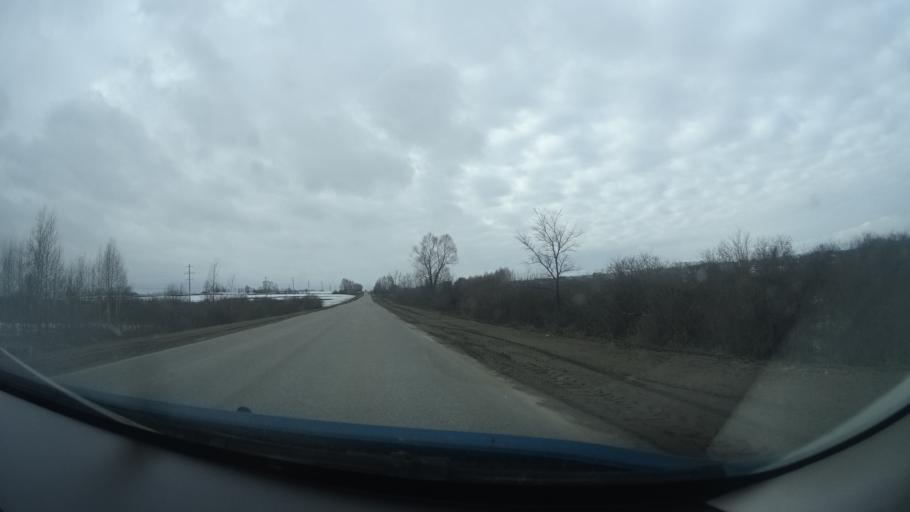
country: RU
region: Bashkortostan
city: Birsk
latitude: 55.4586
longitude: 55.5923
